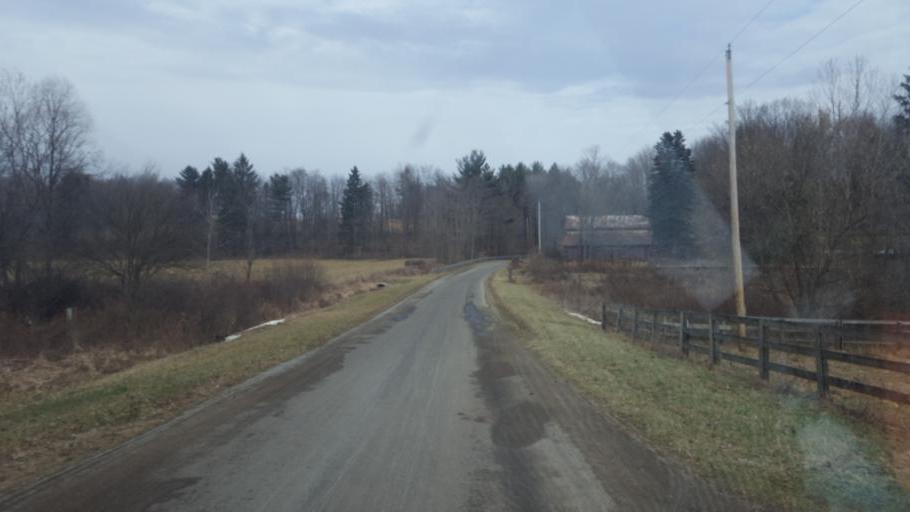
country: US
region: Ohio
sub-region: Richland County
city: Lexington
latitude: 40.5724
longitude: -82.6216
